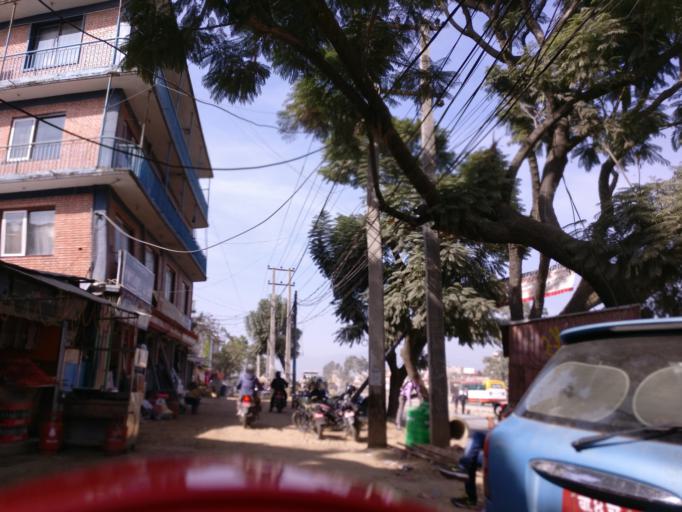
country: NP
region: Central Region
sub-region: Bagmati Zone
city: Patan
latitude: 27.6627
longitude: 85.3161
